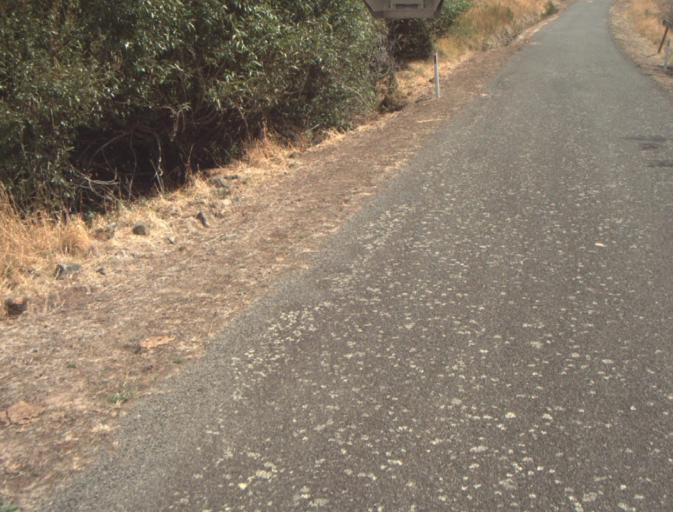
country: AU
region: Tasmania
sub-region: Northern Midlands
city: Evandale
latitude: -41.5163
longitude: 147.4716
